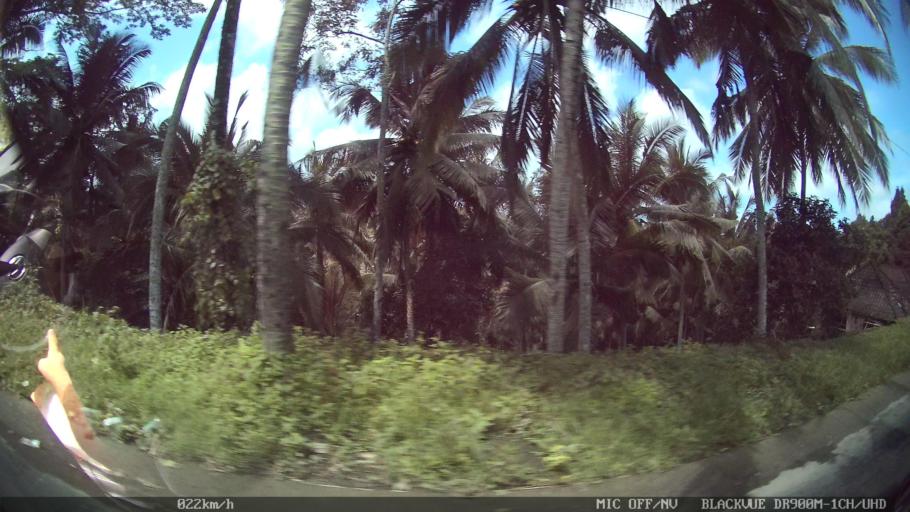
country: ID
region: Bali
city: Banjar Apuan Kaja
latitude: -8.4990
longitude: 115.3412
